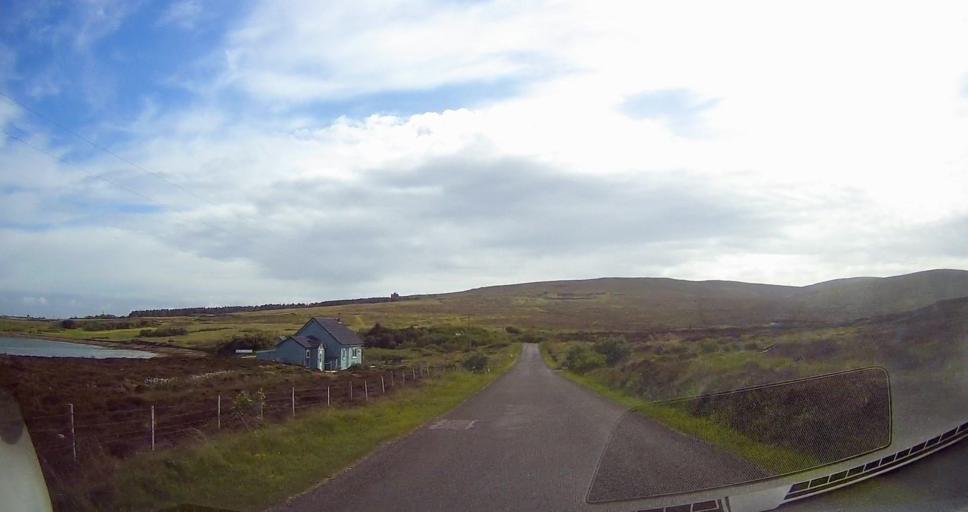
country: GB
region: Scotland
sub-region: Orkney Islands
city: Stromness
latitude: 58.8424
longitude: -3.2127
